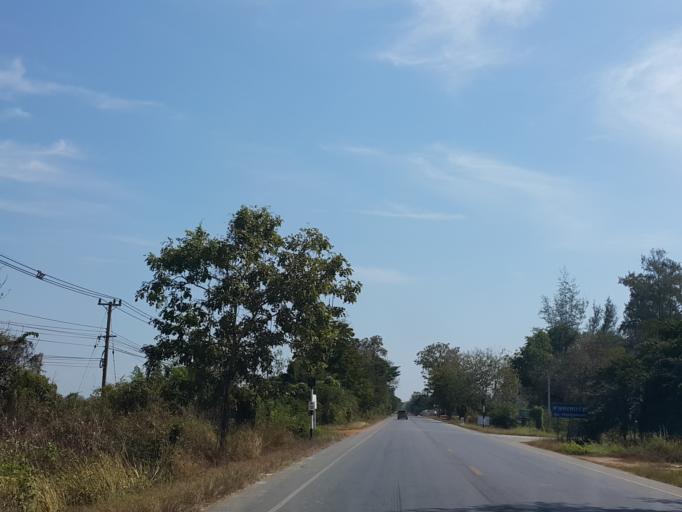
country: TH
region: Sukhothai
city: Sawankhalok
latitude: 17.3142
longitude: 99.6996
